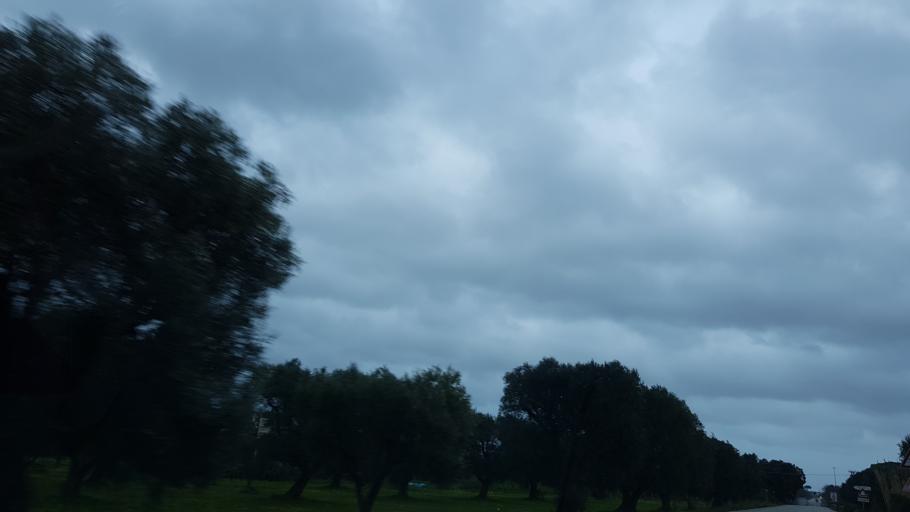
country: IT
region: Apulia
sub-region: Provincia di Brindisi
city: Brindisi
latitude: 40.6491
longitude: 17.8525
